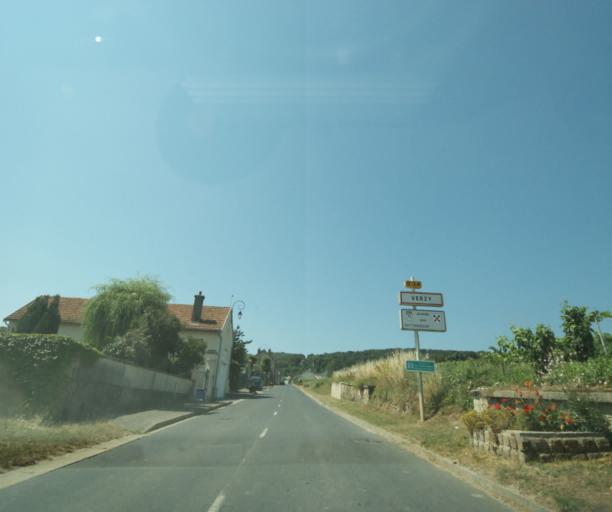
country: FR
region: Champagne-Ardenne
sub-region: Departement de la Marne
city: Verzy
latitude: 49.1498
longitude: 4.1710
